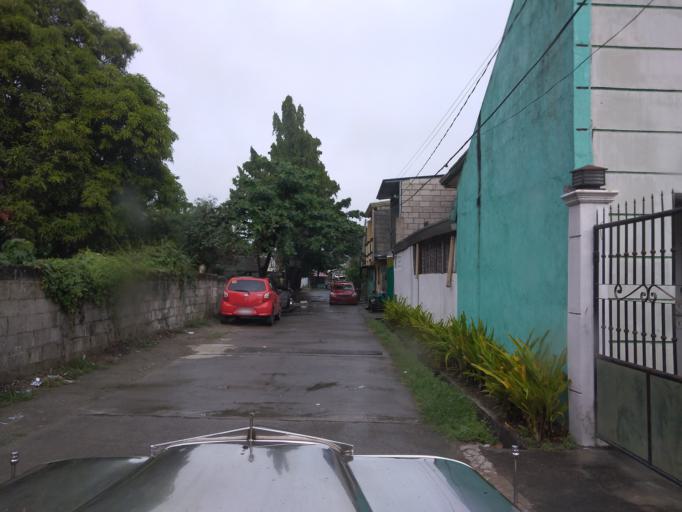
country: PH
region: Central Luzon
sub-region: Province of Pampanga
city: Mexico
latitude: 15.0653
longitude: 120.7224
